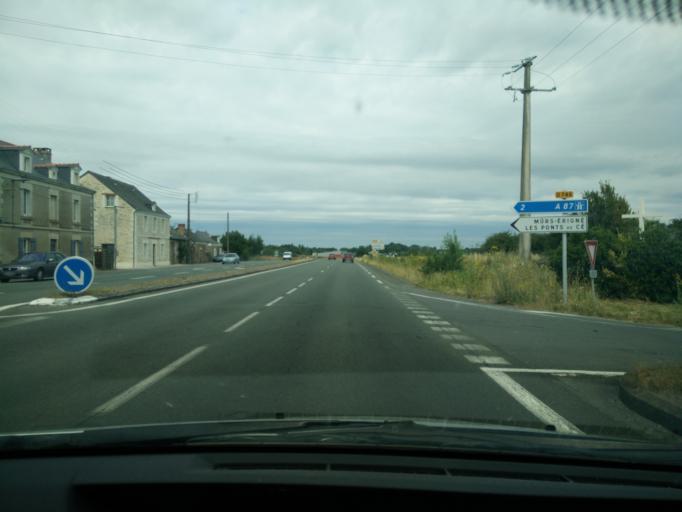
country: FR
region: Pays de la Loire
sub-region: Departement de Maine-et-Loire
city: Saint-Melaine-sur-Aubance
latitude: 47.3879
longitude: -0.4935
